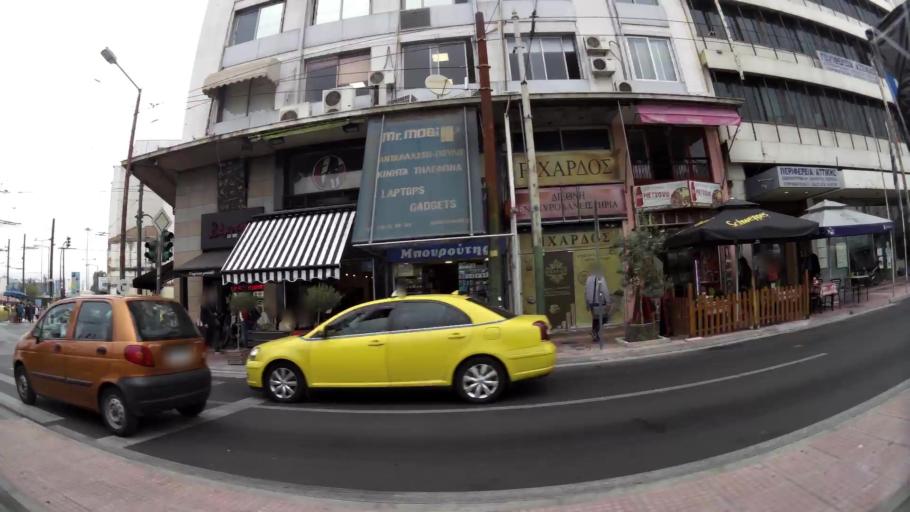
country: GR
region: Attica
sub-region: Nomos Attikis
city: Piraeus
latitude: 37.9453
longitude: 23.6427
